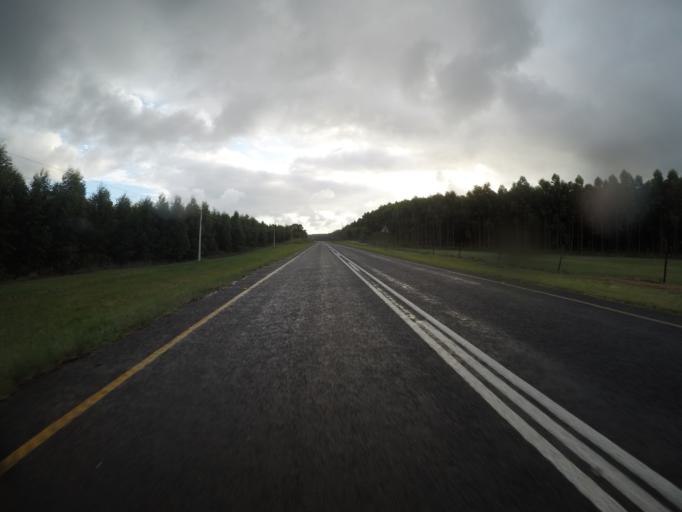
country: ZA
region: KwaZulu-Natal
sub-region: uMkhanyakude District Municipality
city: Mtubatuba
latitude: -28.3683
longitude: 32.2596
